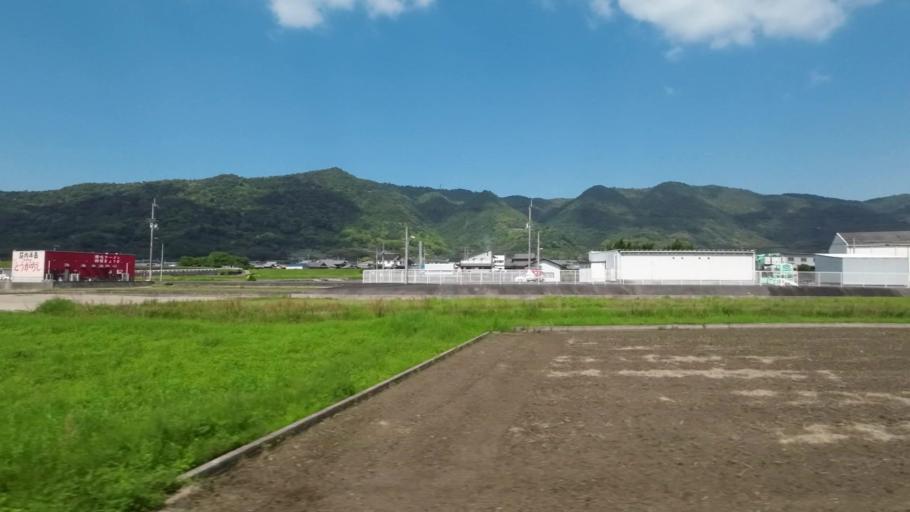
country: JP
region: Kagawa
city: Kan'onjicho
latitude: 34.1609
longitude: 133.6892
